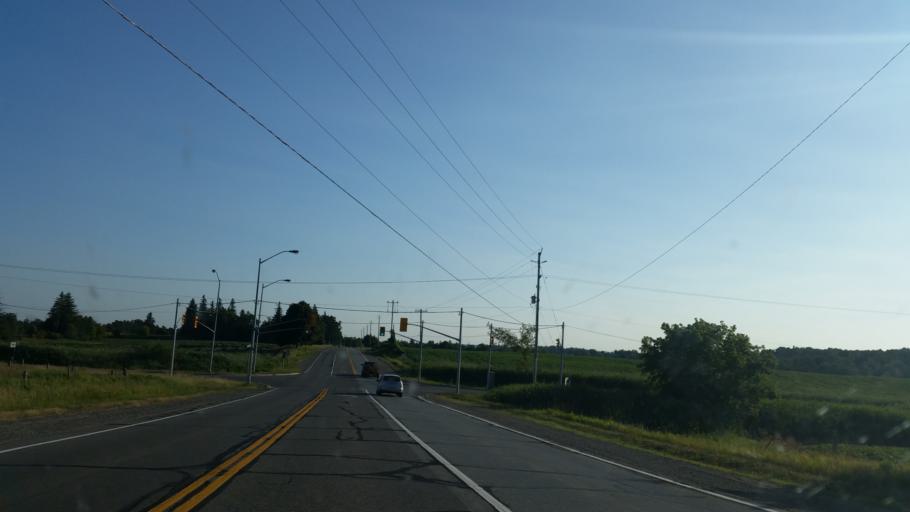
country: CA
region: Ontario
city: Brampton
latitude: 43.7931
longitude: -79.8562
